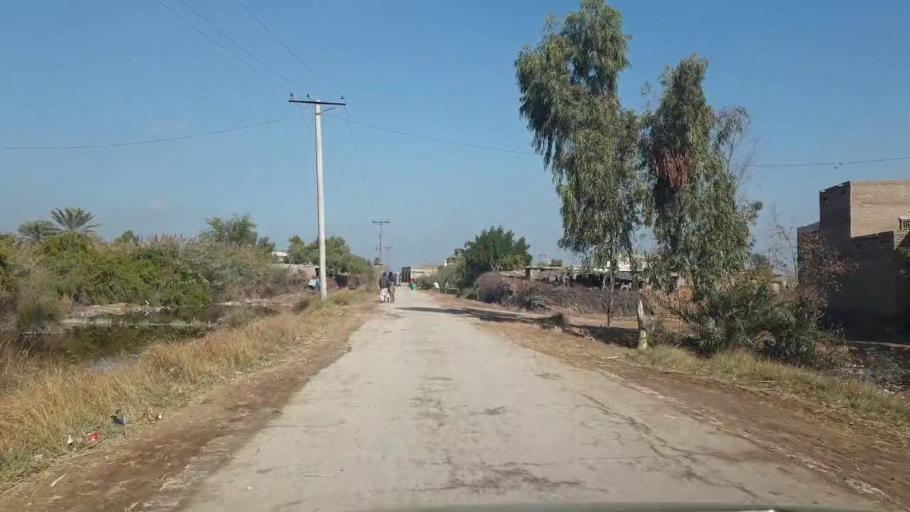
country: PK
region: Sindh
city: Shahdadpur
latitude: 25.9066
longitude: 68.5958
